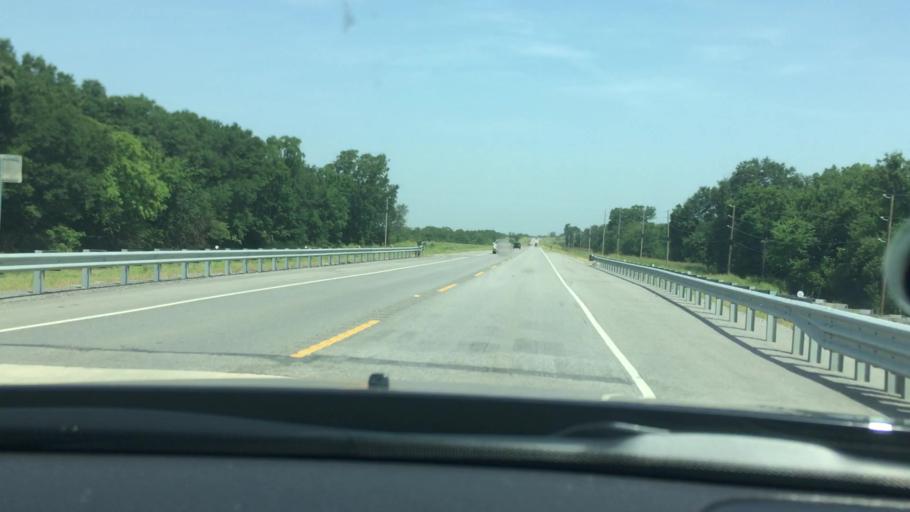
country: US
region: Oklahoma
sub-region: Coal County
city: Coalgate
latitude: 34.4457
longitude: -96.2068
